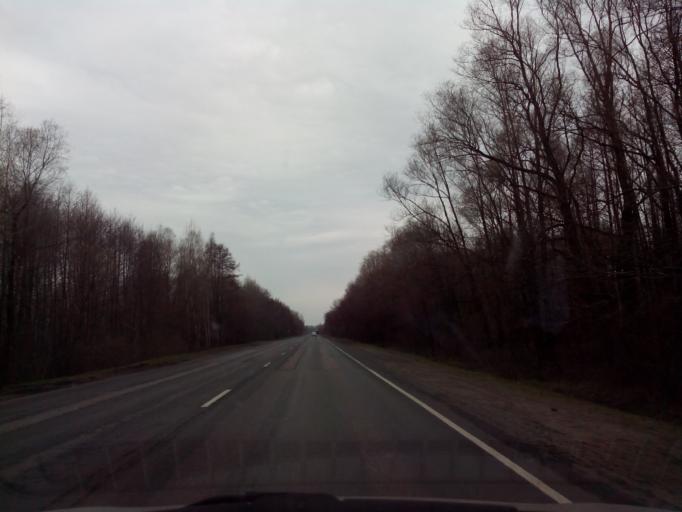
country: RU
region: Tambov
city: Zavoronezhskoye
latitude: 52.9352
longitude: 40.6065
